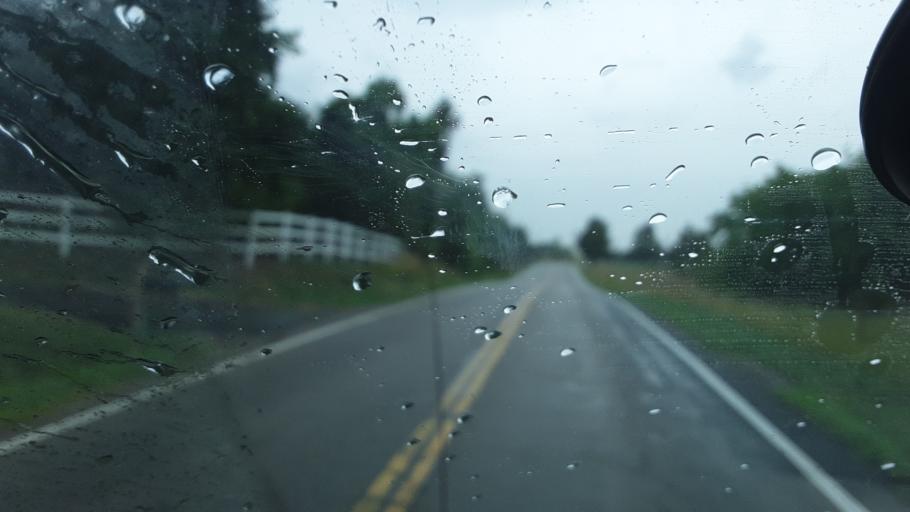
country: US
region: Ohio
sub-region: Williams County
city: Bryan
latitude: 41.5120
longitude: -84.6131
